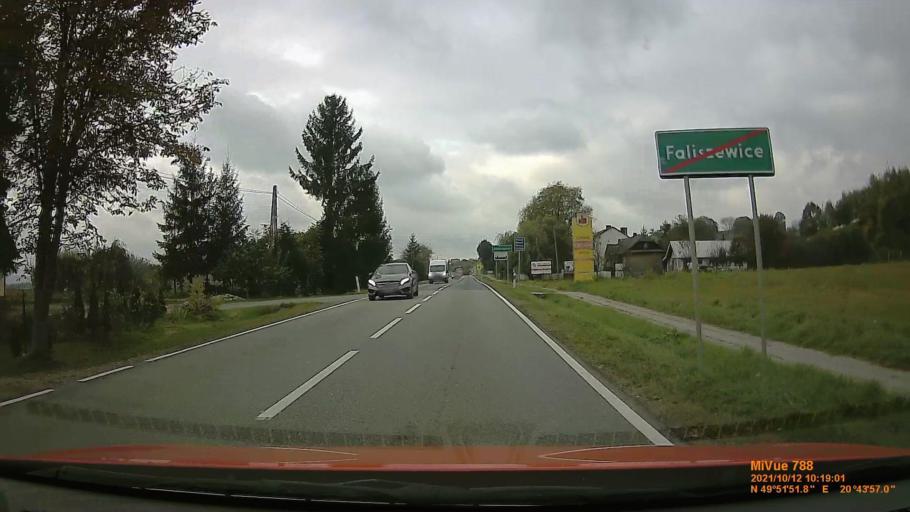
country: PL
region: Lesser Poland Voivodeship
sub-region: Powiat brzeski
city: Zlota
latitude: 49.8644
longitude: 20.7322
